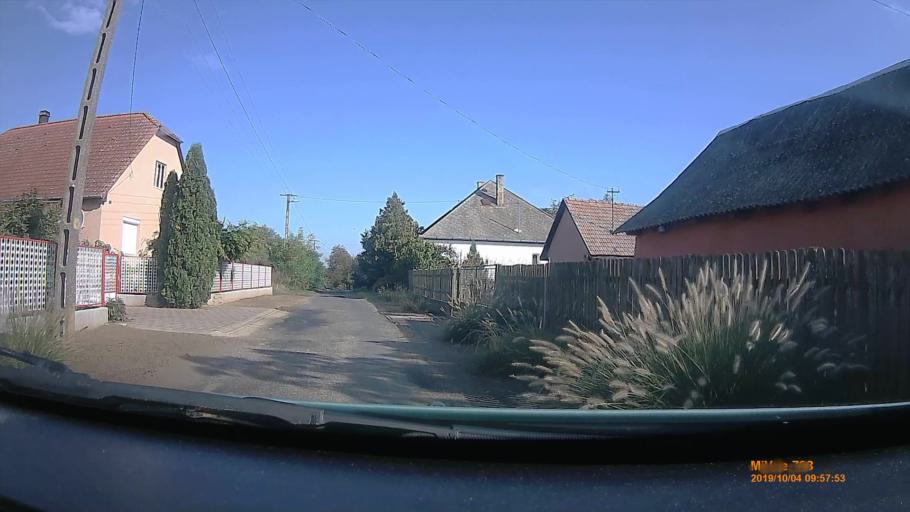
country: HU
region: Szabolcs-Szatmar-Bereg
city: Nyiregyhaza
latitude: 47.9410
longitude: 21.6635
